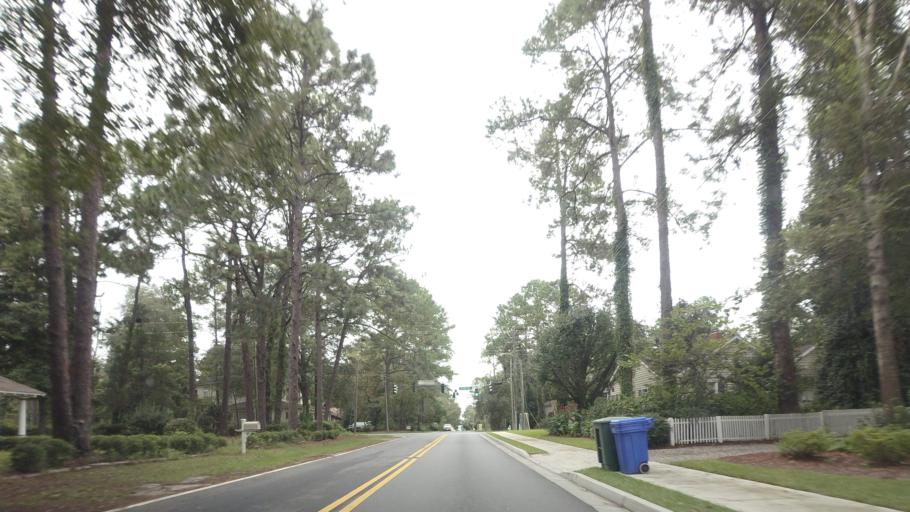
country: US
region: Georgia
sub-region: Lowndes County
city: Remerton
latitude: 30.8536
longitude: -83.2927
